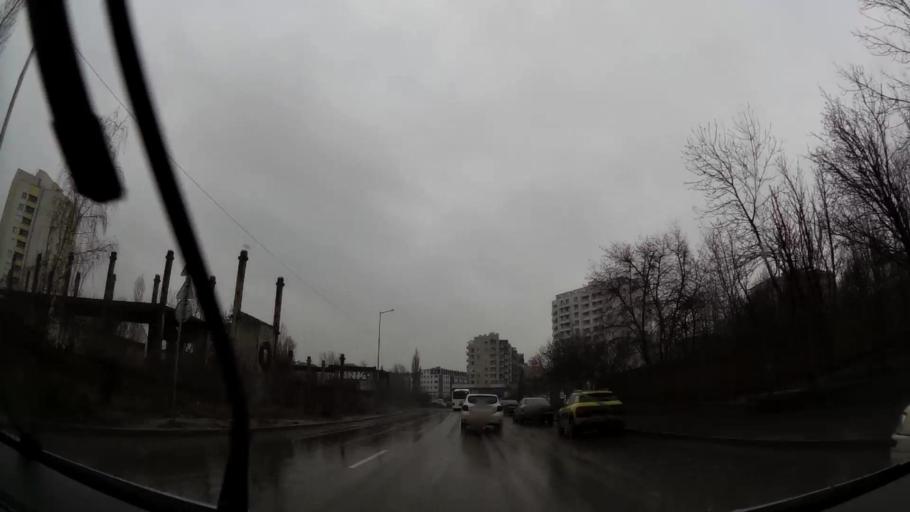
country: BG
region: Sofia-Capital
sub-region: Stolichna Obshtina
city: Sofia
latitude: 42.6473
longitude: 23.3417
